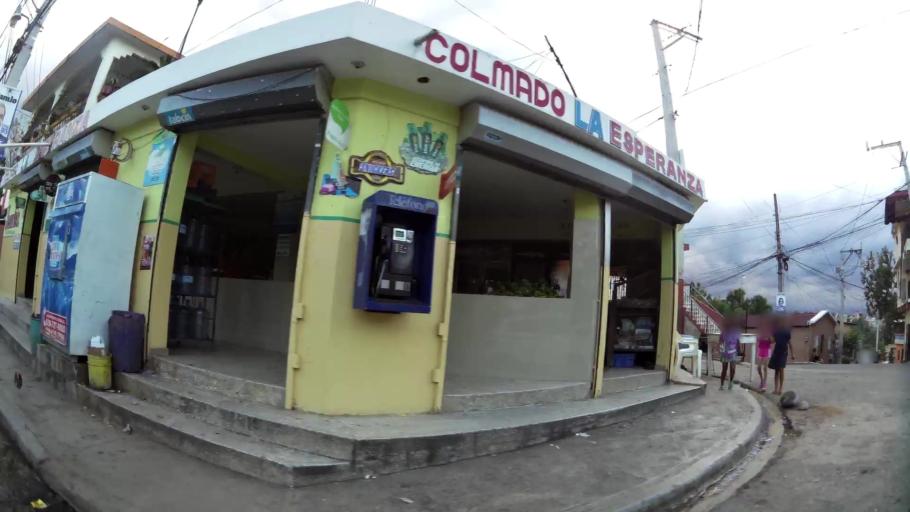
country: DO
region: Santo Domingo
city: Santo Domingo Oeste
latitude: 18.5268
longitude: -70.0189
